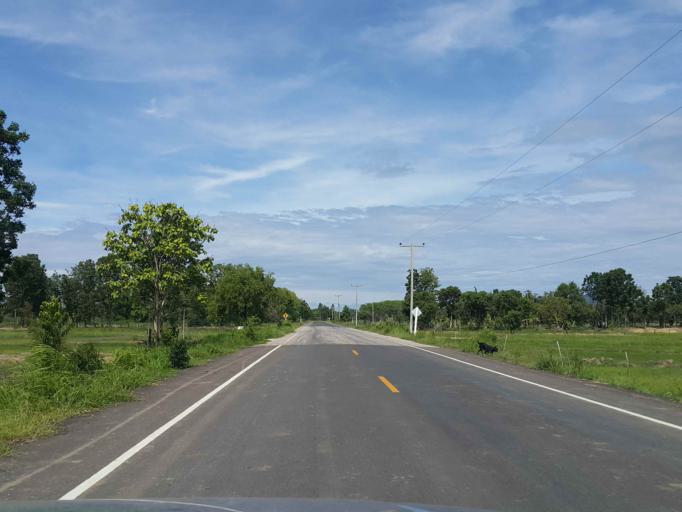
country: TH
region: Sukhothai
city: Ban Dan Lan Hoi
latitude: 17.1152
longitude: 99.5296
